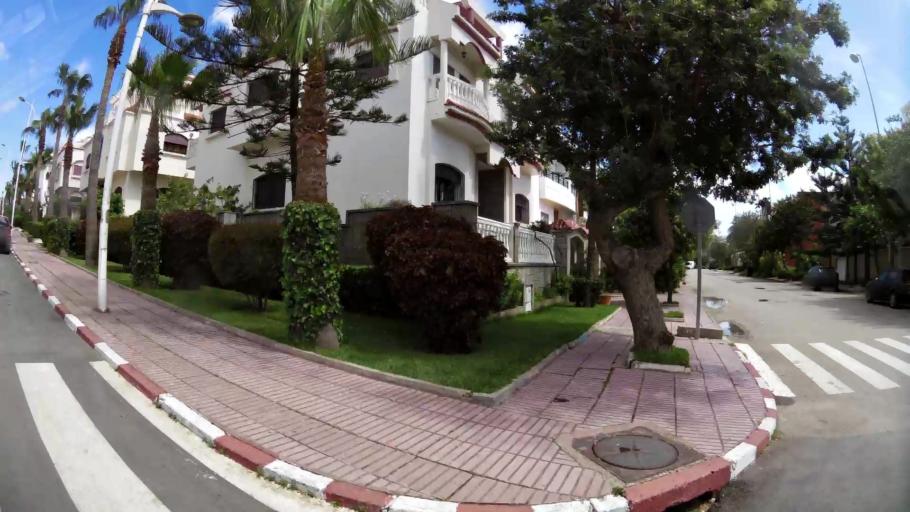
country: MA
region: Tanger-Tetouan
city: Tetouan
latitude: 35.5880
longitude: -5.3377
